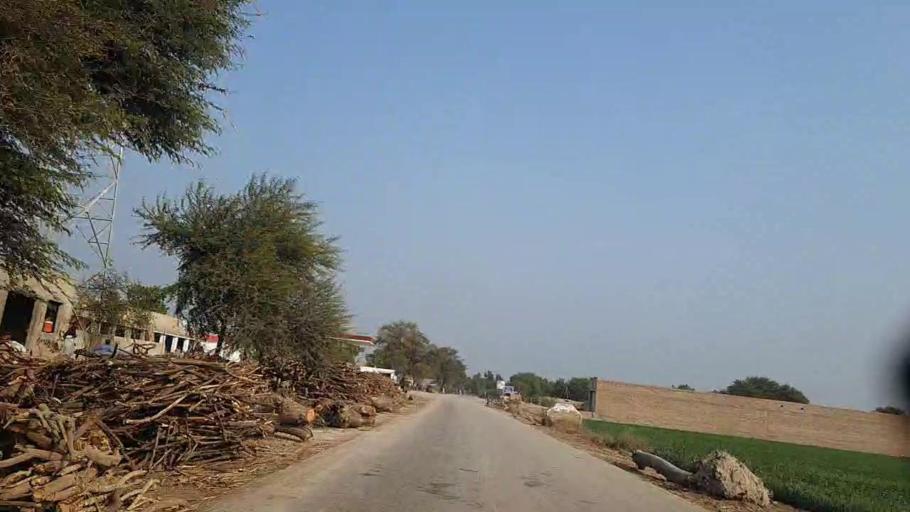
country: PK
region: Sindh
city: Sakrand
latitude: 26.1323
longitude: 68.2138
